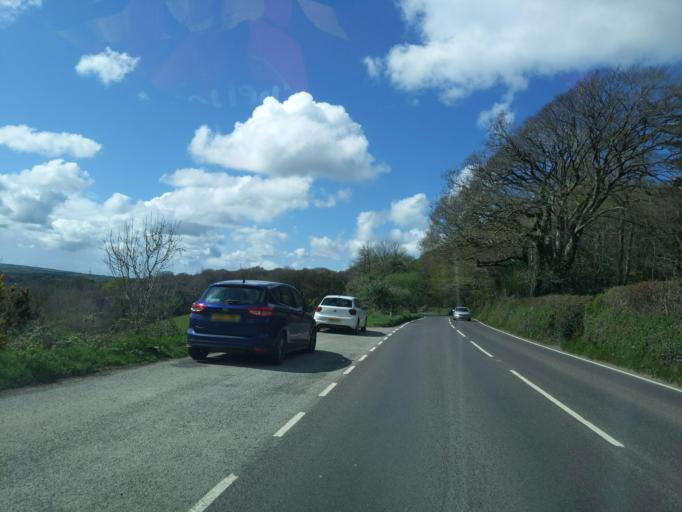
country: GB
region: England
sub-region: Cornwall
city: Bodmin
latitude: 50.4967
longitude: -4.7712
